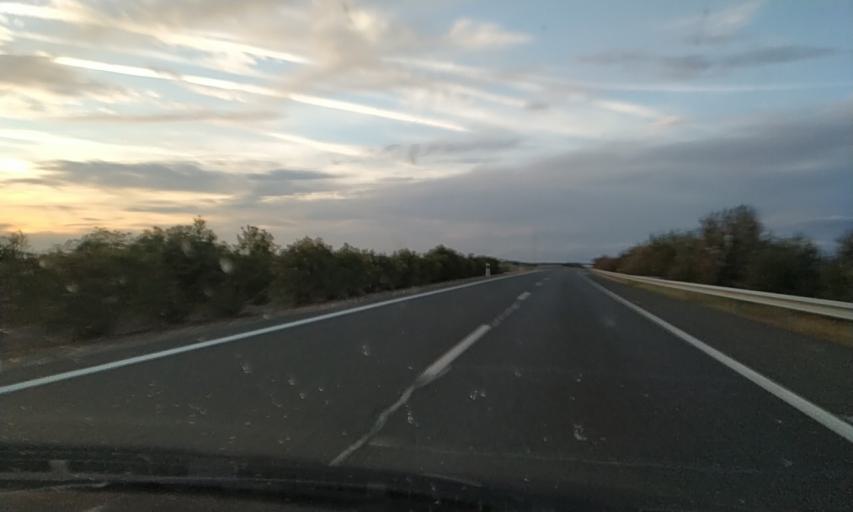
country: ES
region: Extremadura
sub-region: Provincia de Caceres
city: Aldea del Cano
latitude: 39.3207
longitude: -6.3292
